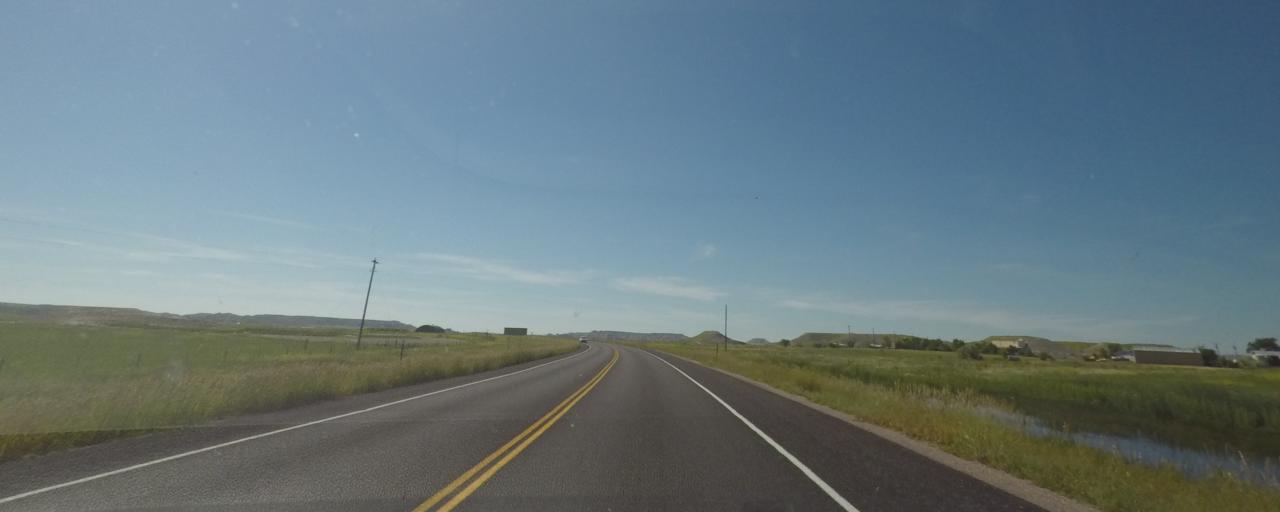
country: US
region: South Dakota
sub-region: Shannon County
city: Porcupine
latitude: 43.7830
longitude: -102.5536
